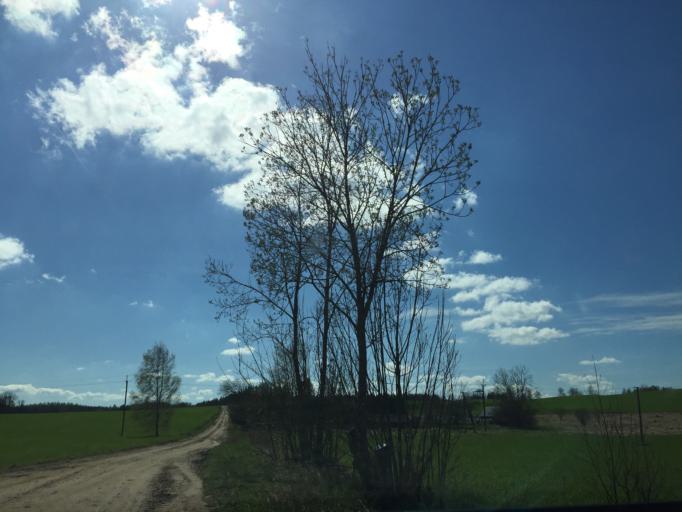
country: EE
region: Valgamaa
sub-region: Valga linn
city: Valga
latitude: 57.9100
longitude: 26.0397
